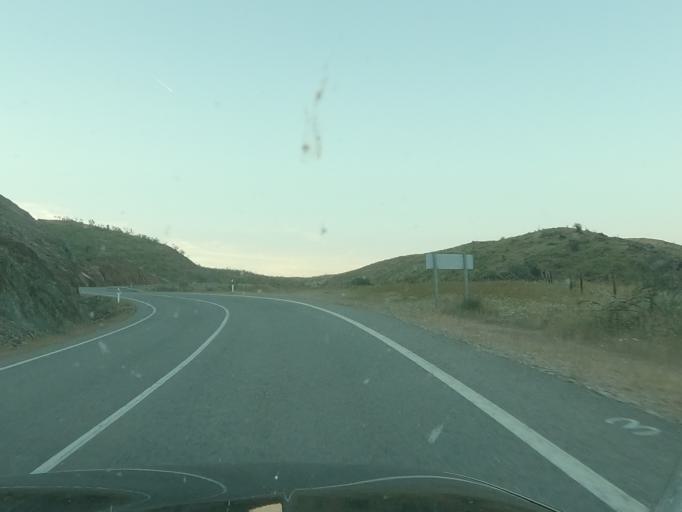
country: ES
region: Extremadura
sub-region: Provincia de Caceres
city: Salorino
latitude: 39.5842
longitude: -6.9966
